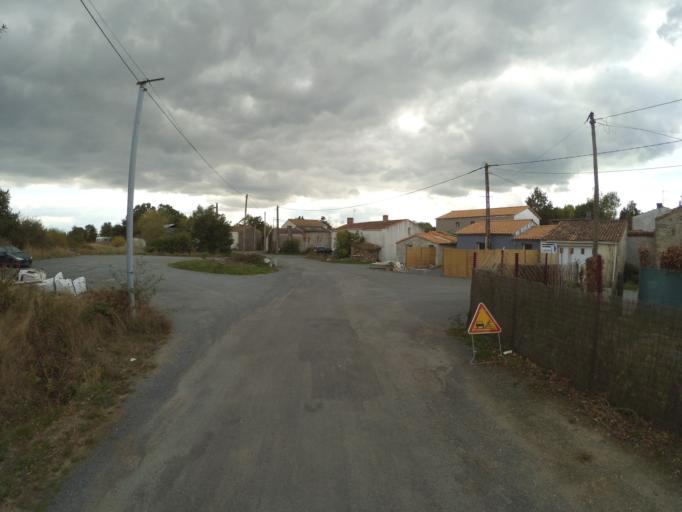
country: FR
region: Pays de la Loire
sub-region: Departement de la Loire-Atlantique
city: Remouille
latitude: 47.0619
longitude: -1.3705
